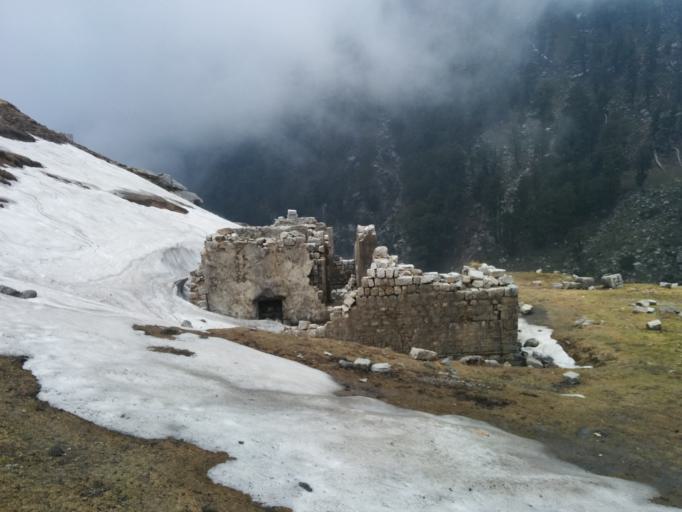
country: IN
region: Himachal Pradesh
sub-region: Kangra
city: Dharmsala
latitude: 32.2813
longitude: 76.3636
